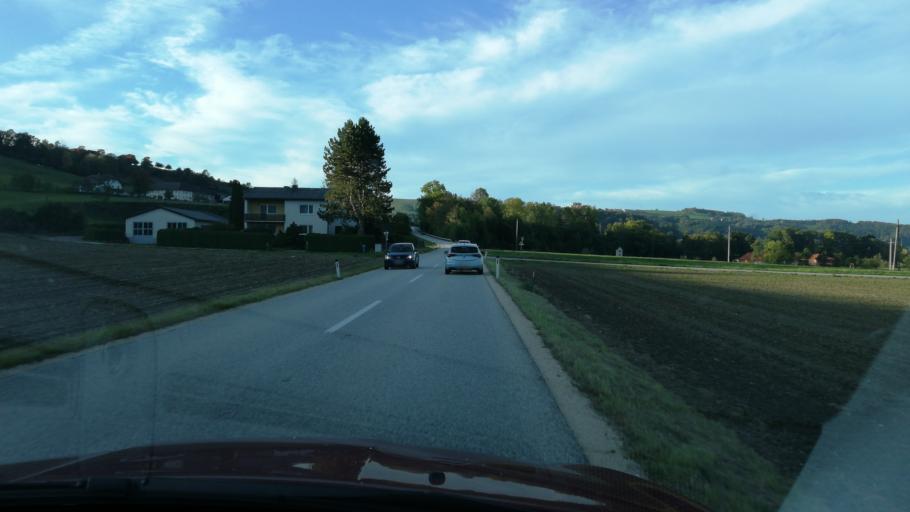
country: AT
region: Upper Austria
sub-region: Politischer Bezirk Steyr-Land
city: Ternberg
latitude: 47.9618
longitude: 14.3480
